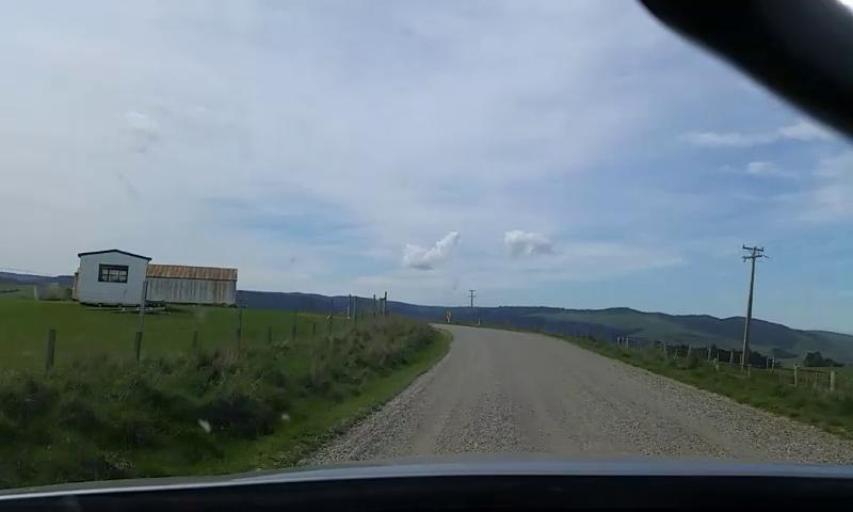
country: NZ
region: Otago
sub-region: Clutha District
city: Papatowai
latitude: -46.6310
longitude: 168.9804
